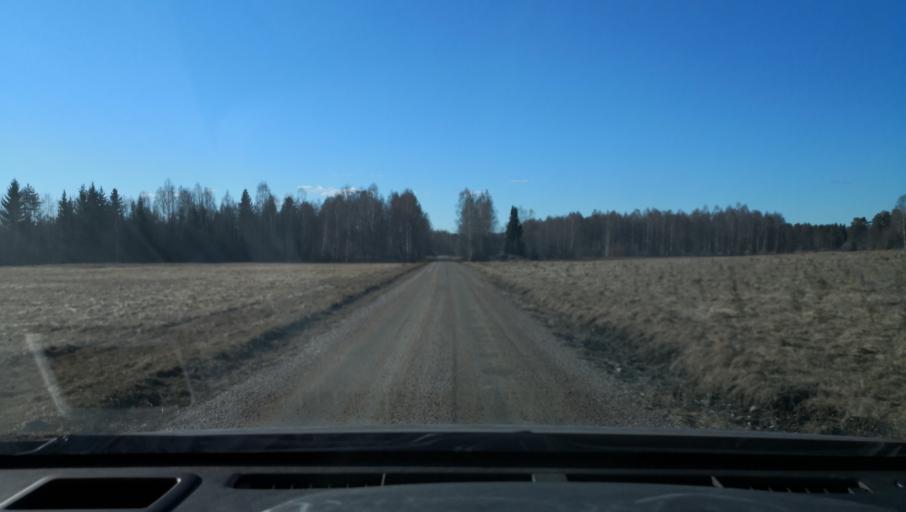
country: SE
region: Vaestmanland
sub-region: Sala Kommun
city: Sala
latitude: 60.1205
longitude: 16.6643
